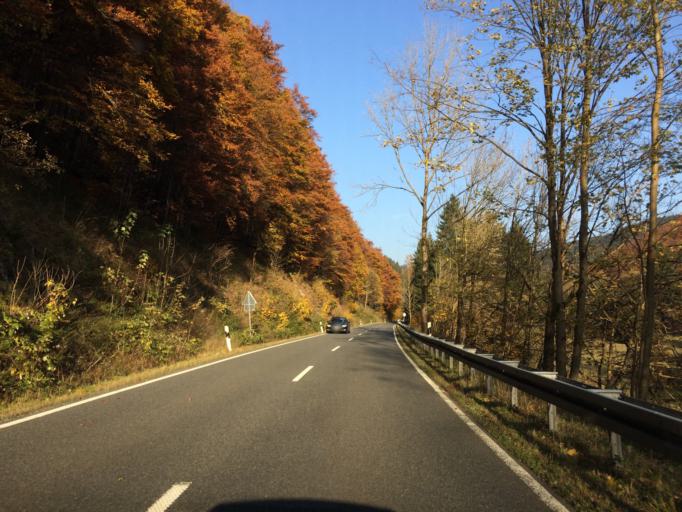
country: DE
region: Lower Saxony
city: Sankt Andreasberg
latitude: 51.6725
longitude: 10.5511
